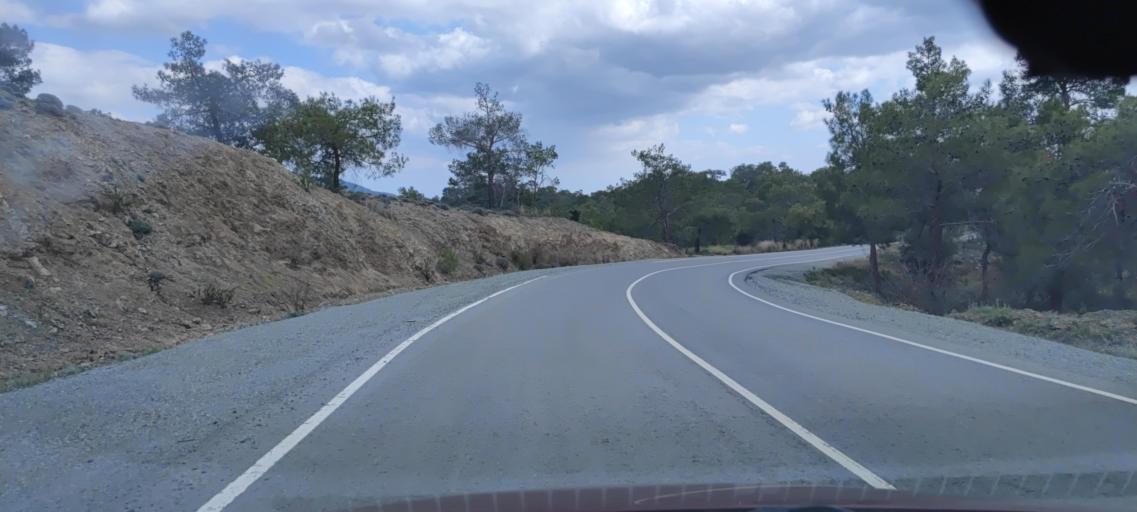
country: CY
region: Lefkosia
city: Lythrodontas
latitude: 34.9392
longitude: 33.3248
